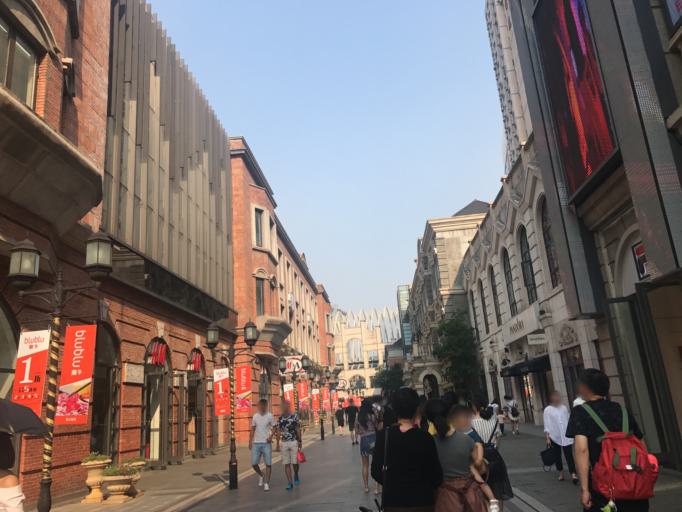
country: CN
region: Hubei
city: Jiang'an
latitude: 30.5585
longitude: 114.3367
